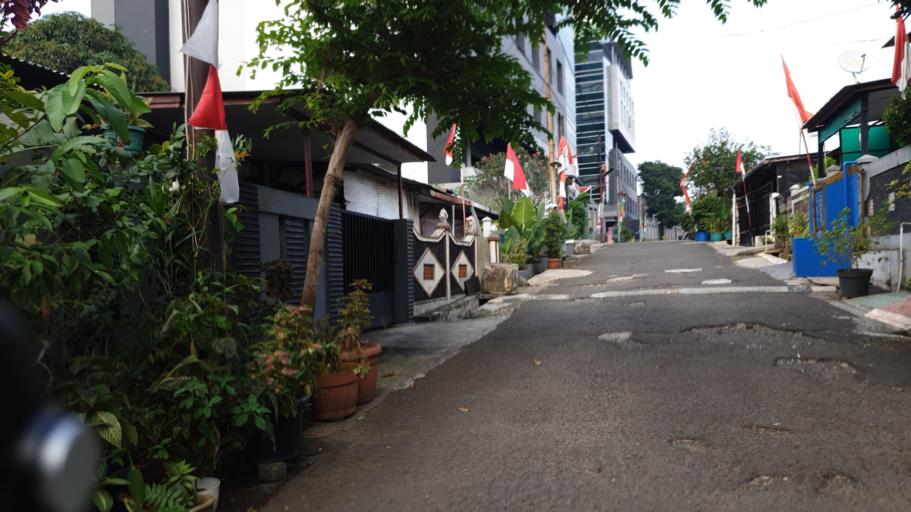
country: ID
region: West Java
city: Depok
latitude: -6.3702
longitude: 106.8393
